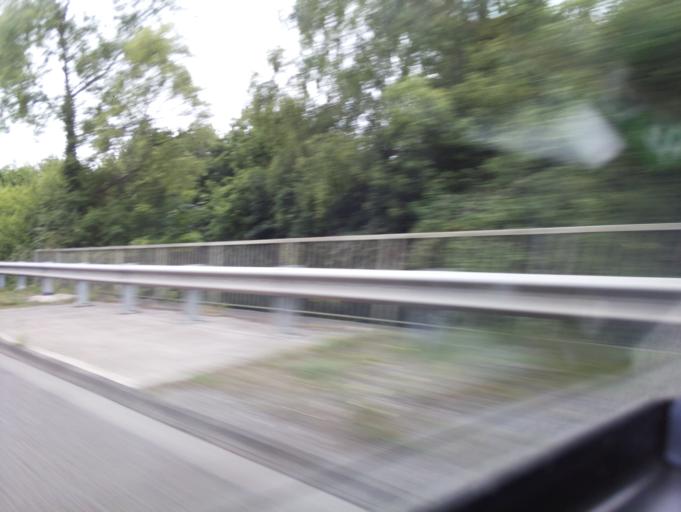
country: GB
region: England
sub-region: Worcestershire
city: Droitwich
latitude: 52.2722
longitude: -2.1635
